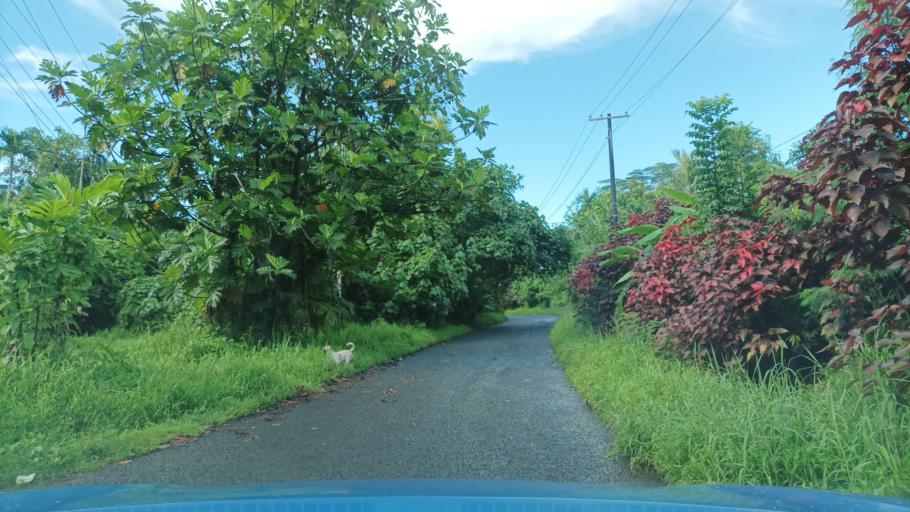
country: FM
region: Pohnpei
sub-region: Kolonia Municipality
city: Kolonia Town
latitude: 6.9373
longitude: 158.1921
